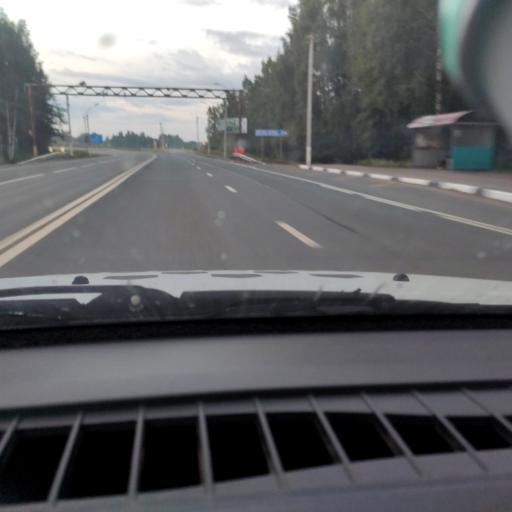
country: RU
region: Kirov
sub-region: Kirovo-Chepetskiy Rayon
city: Kirov
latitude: 58.6775
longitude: 49.6480
